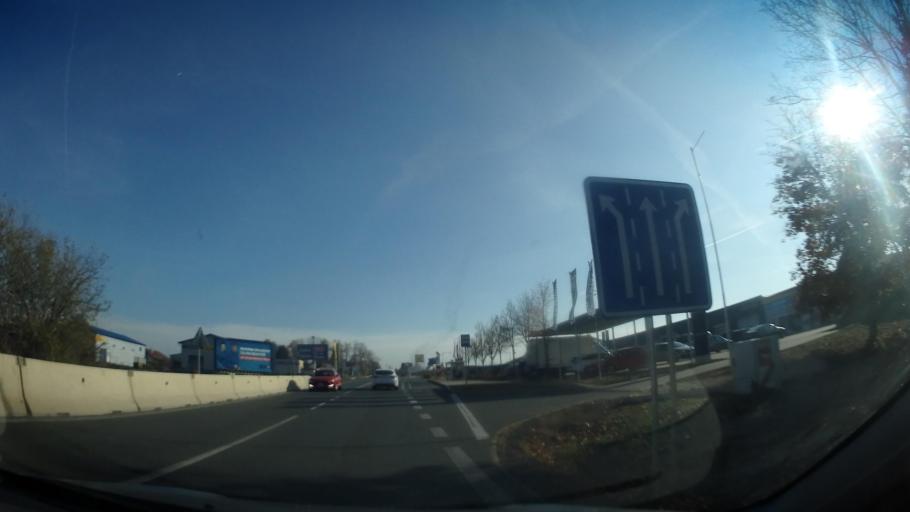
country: CZ
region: Central Bohemia
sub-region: Okres Praha-Vychod
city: Ricany
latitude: 50.0052
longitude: 14.6565
